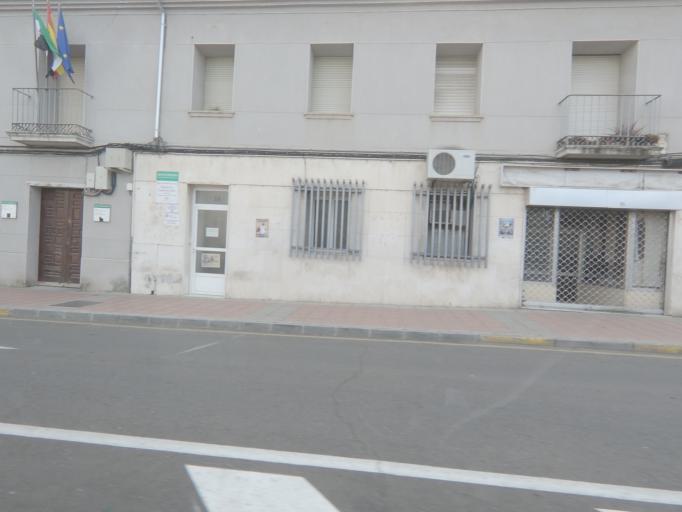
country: ES
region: Extremadura
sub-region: Provincia de Caceres
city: Coria
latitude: 39.9881
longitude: -6.5384
